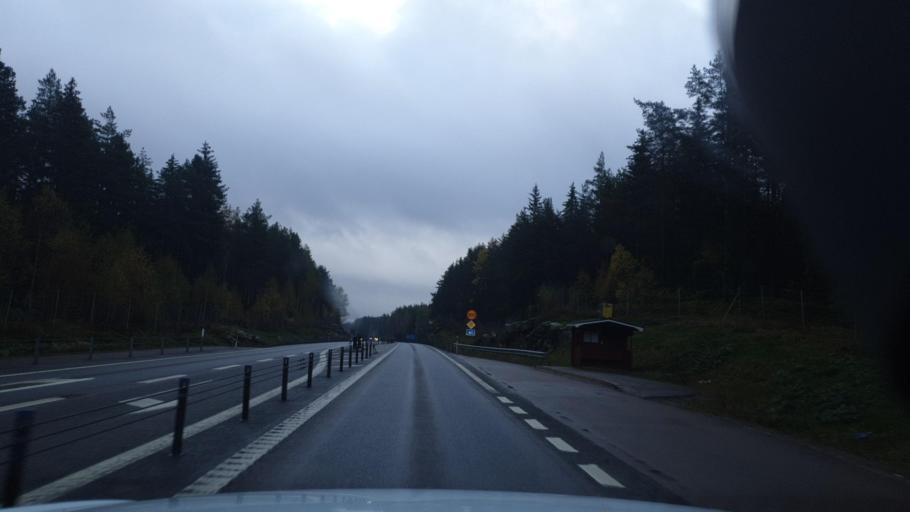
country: SE
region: Vaermland
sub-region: Arvika Kommun
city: Arvika
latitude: 59.6475
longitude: 12.6959
